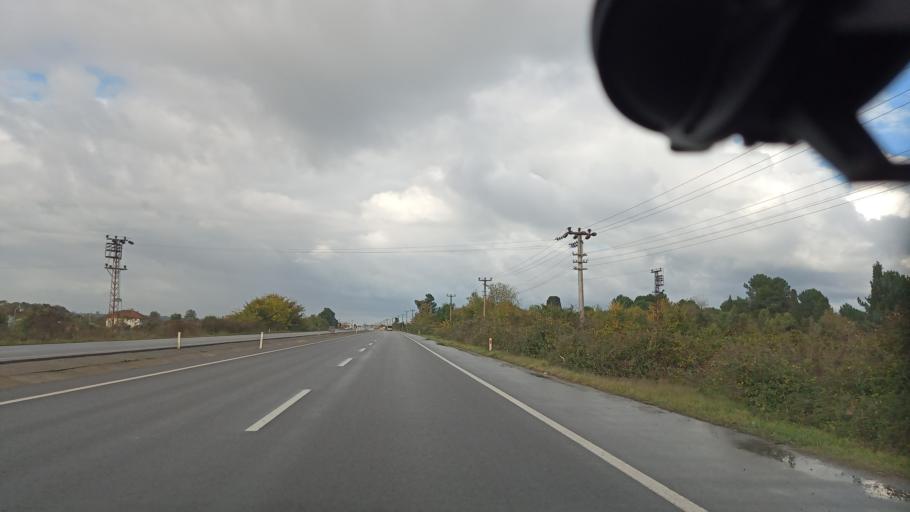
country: TR
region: Sakarya
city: Karasu
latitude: 41.0772
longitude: 30.7787
